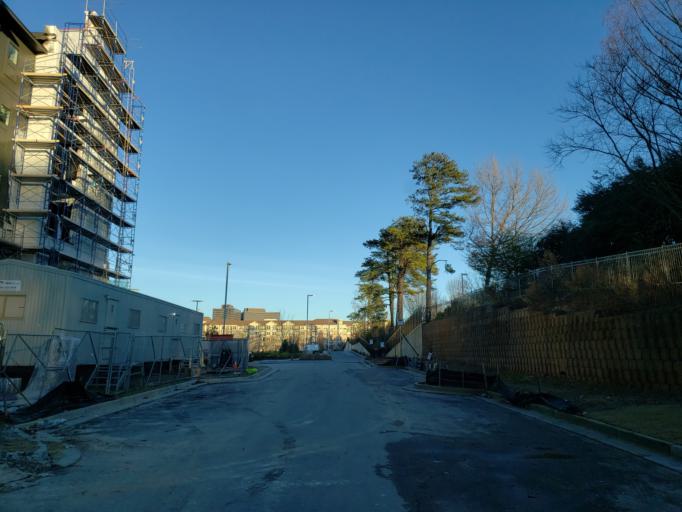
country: US
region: Georgia
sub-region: Fulton County
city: Sandy Springs
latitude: 33.9325
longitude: -84.3649
